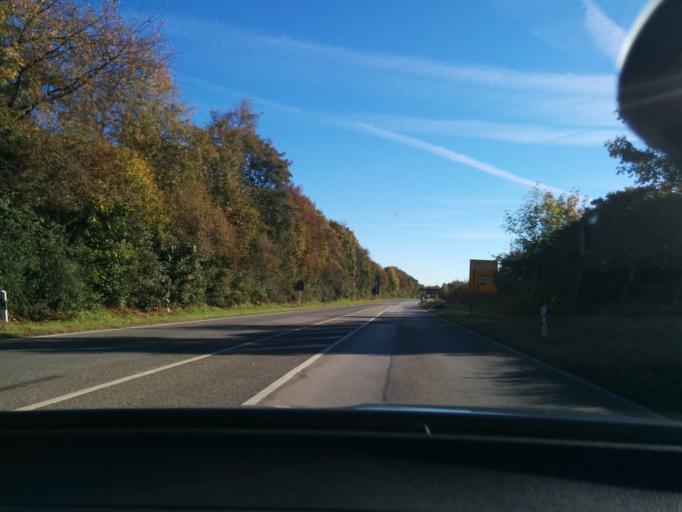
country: DE
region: Bavaria
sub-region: Upper Bavaria
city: Kirchheim bei Muenchen
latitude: 48.1708
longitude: 11.7470
